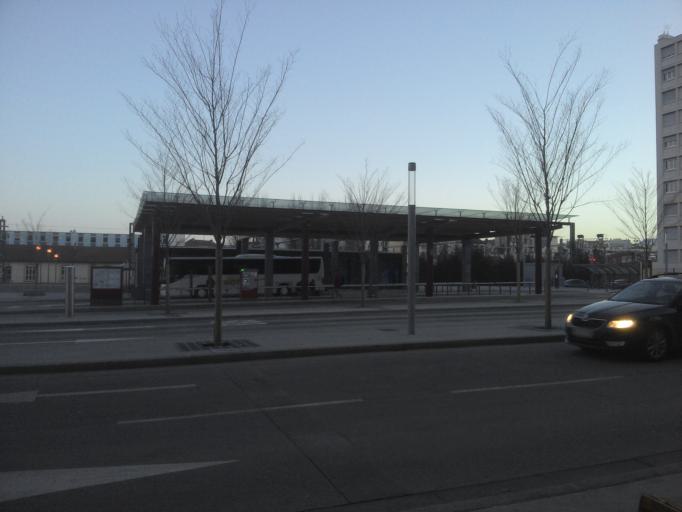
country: FR
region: Auvergne
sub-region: Departement du Puy-de-Dome
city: Clermont-Ferrand
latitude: 45.7786
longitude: 3.0989
